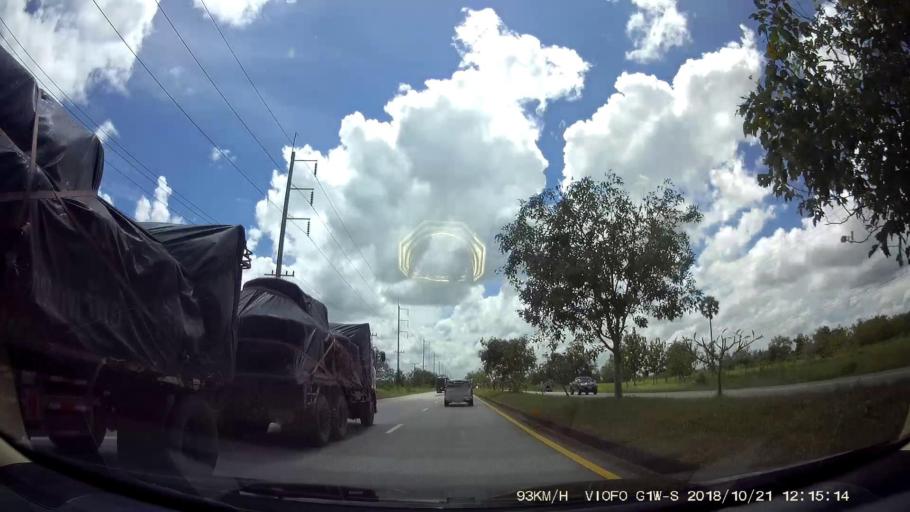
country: TH
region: Nakhon Ratchasima
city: Dan Khun Thot
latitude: 15.3654
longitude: 101.8314
